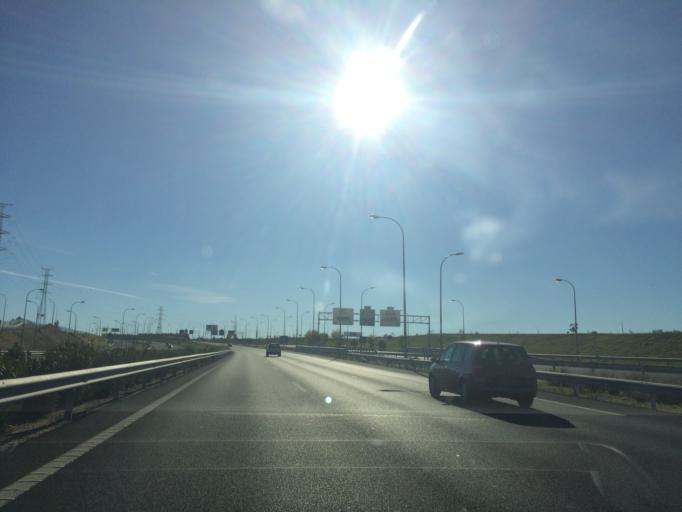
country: ES
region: Madrid
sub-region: Provincia de Madrid
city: Pozuelo de Alarcon
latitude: 40.4027
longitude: -3.8312
